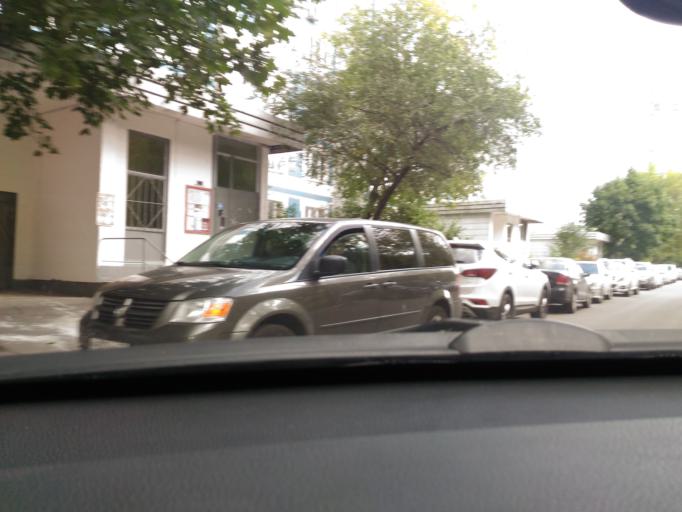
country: RU
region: Moscow
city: Vatutino
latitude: 55.8867
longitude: 37.6989
